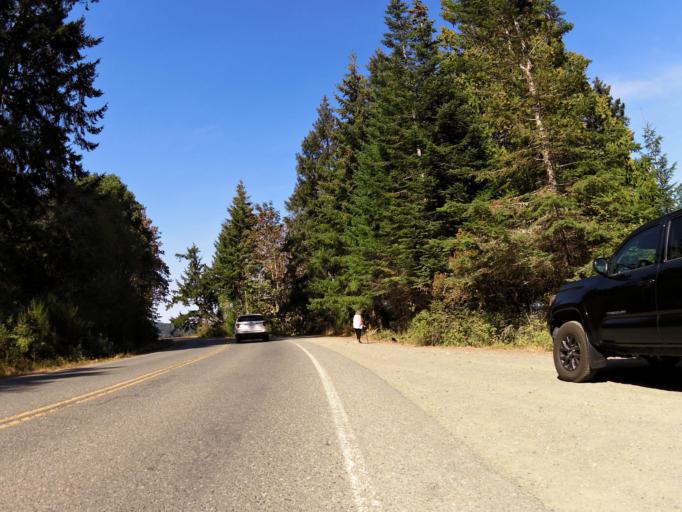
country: CA
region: British Columbia
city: North Saanich
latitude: 48.6315
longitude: -123.5300
